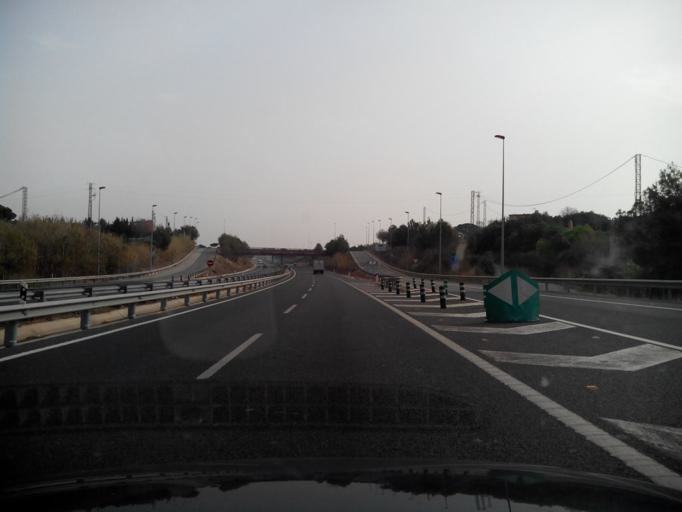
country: ES
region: Catalonia
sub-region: Provincia de Tarragona
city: Reus
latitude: 41.1299
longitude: 1.1171
